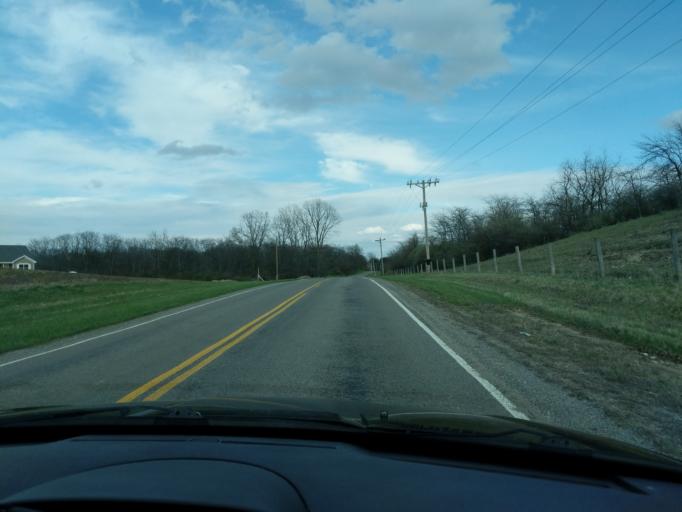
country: US
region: Ohio
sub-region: Champaign County
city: Urbana
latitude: 40.1560
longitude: -83.6669
